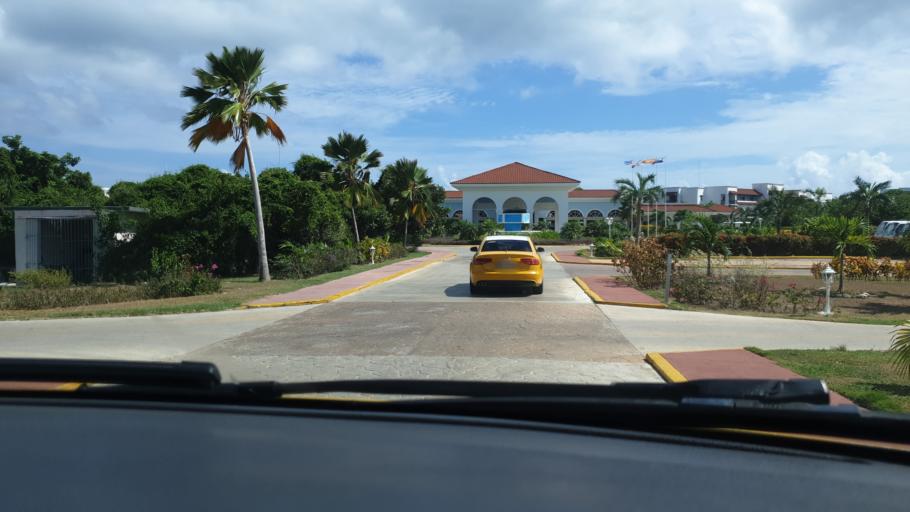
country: CU
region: Sancti Spiritus
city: Yaguajay
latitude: 22.6562
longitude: -79.0297
